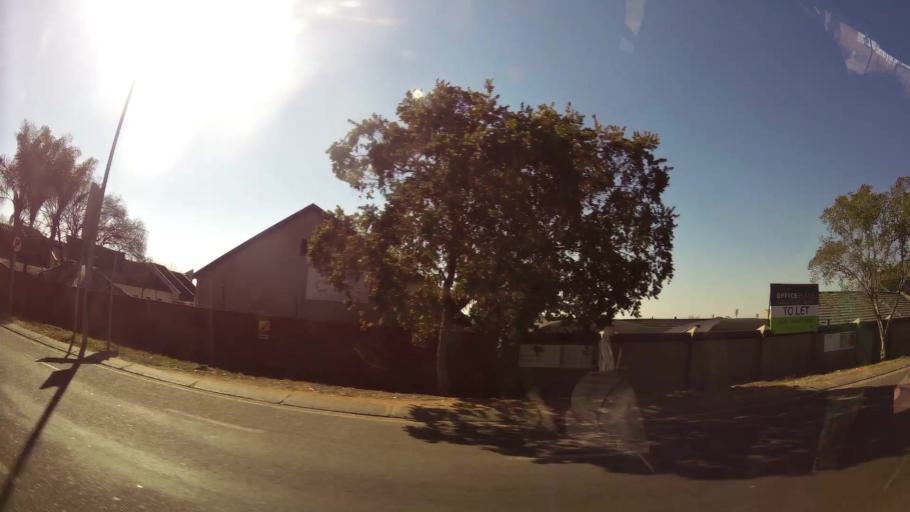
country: ZA
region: Gauteng
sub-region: City of Tshwane Metropolitan Municipality
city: Centurion
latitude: -25.8638
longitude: 28.1887
